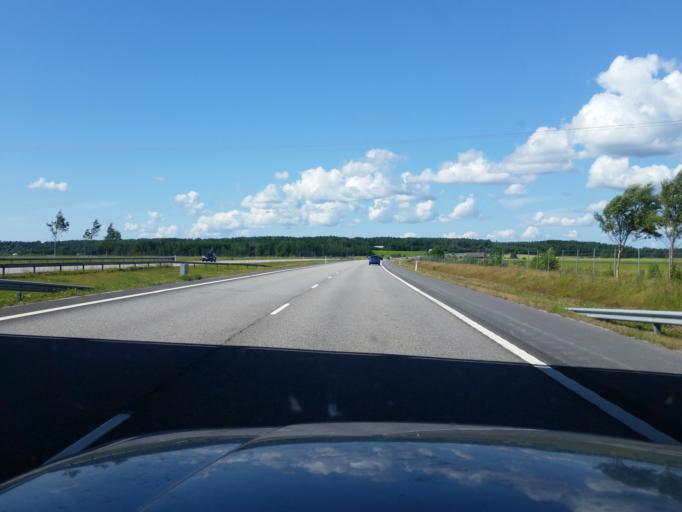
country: FI
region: Varsinais-Suomi
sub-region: Salo
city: Halikko
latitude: 60.4174
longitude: 23.1152
